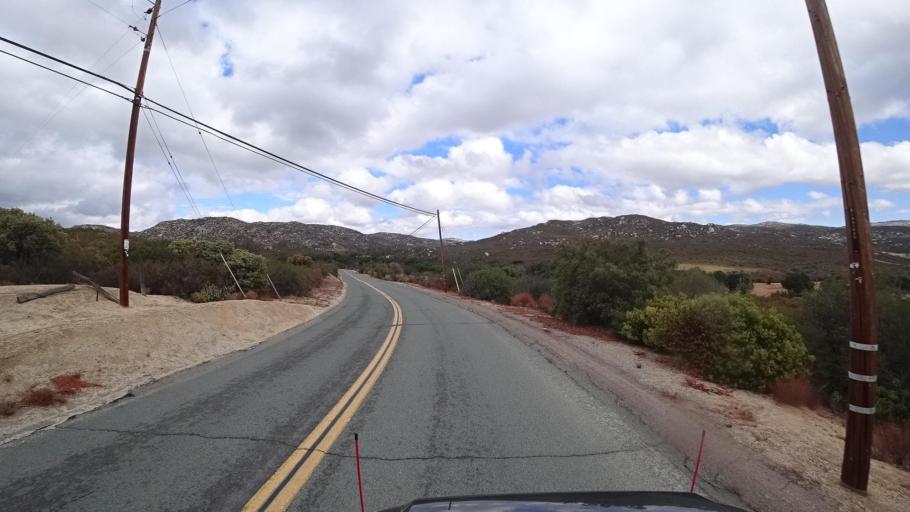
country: US
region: California
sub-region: San Diego County
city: Campo
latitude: 32.6790
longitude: -116.4287
